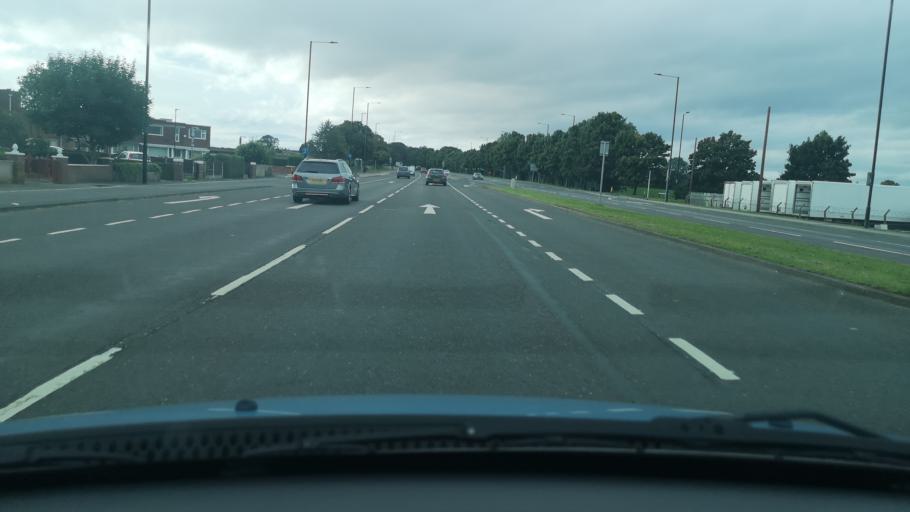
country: GB
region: England
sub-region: Doncaster
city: Bentley
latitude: 53.5412
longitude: -1.1693
